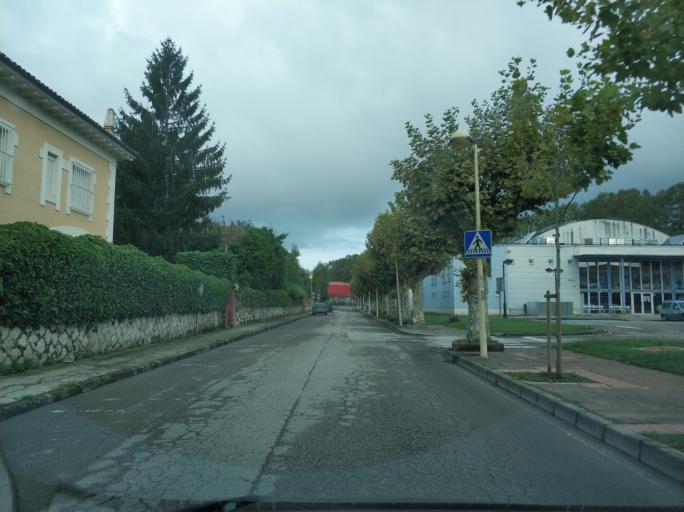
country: ES
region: Cantabria
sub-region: Provincia de Cantabria
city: Torrelavega
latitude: 43.3550
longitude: -4.0571
